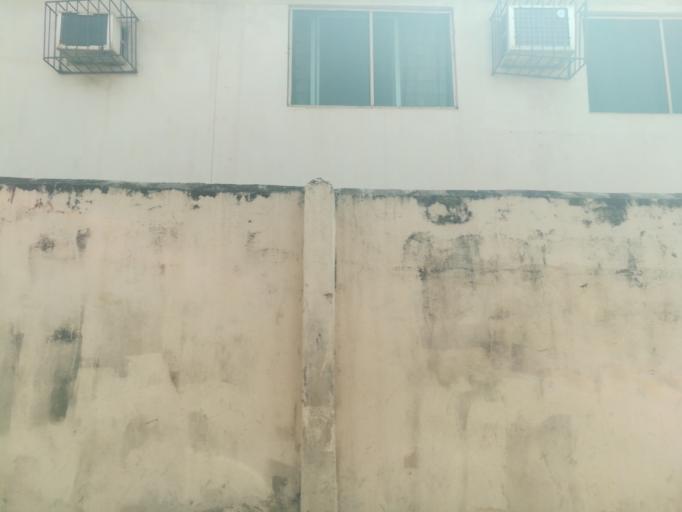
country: NG
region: Oyo
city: Ibadan
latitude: 7.3619
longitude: 3.8791
